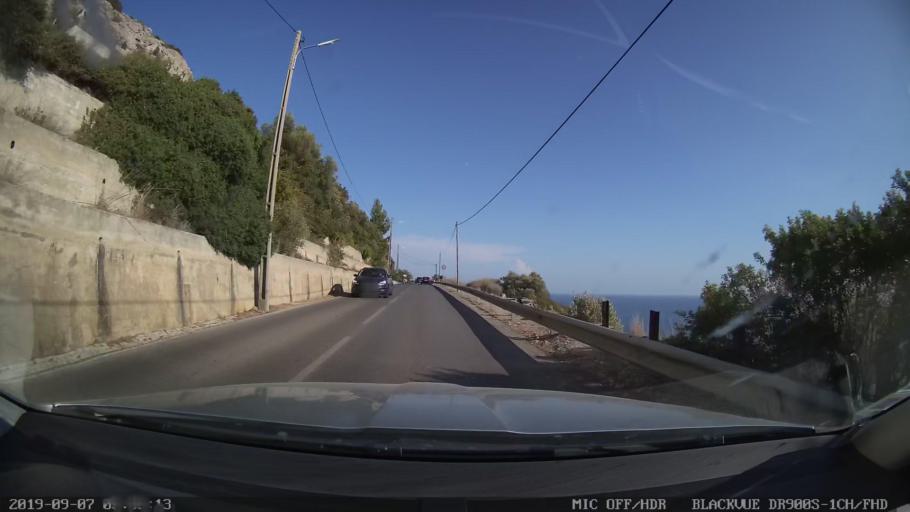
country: PT
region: Setubal
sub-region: Sesimbra
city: Sesimbra
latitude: 38.4425
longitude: -9.0912
